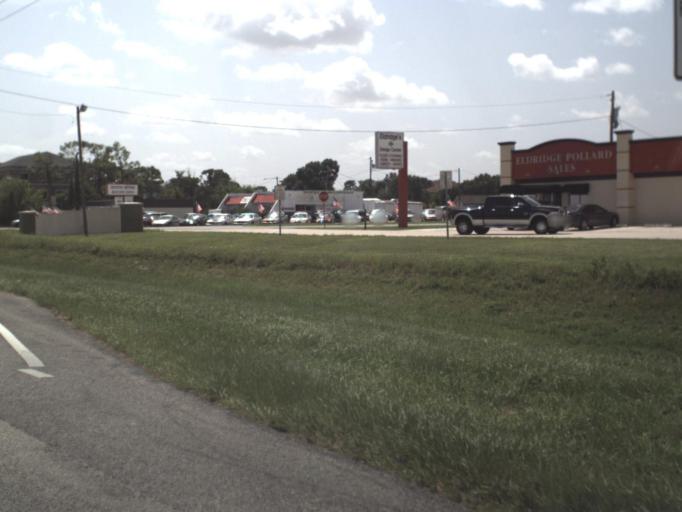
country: US
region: Florida
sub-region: Highlands County
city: Sebring
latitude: 27.4958
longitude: -81.4873
